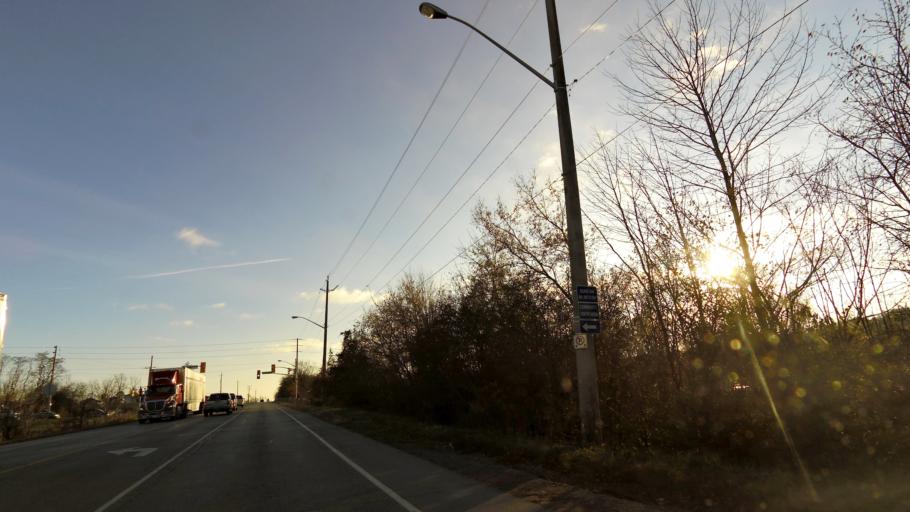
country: CA
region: Ontario
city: Cambridge
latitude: 43.3400
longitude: -80.3134
